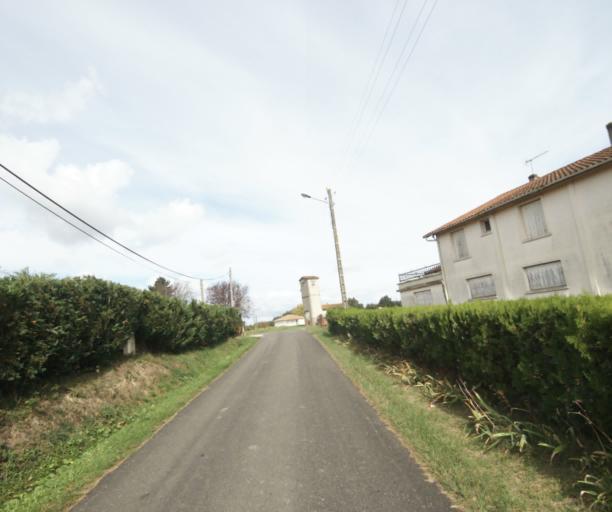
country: FR
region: Midi-Pyrenees
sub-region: Departement du Gers
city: Eauze
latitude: 43.8585
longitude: 0.0814
